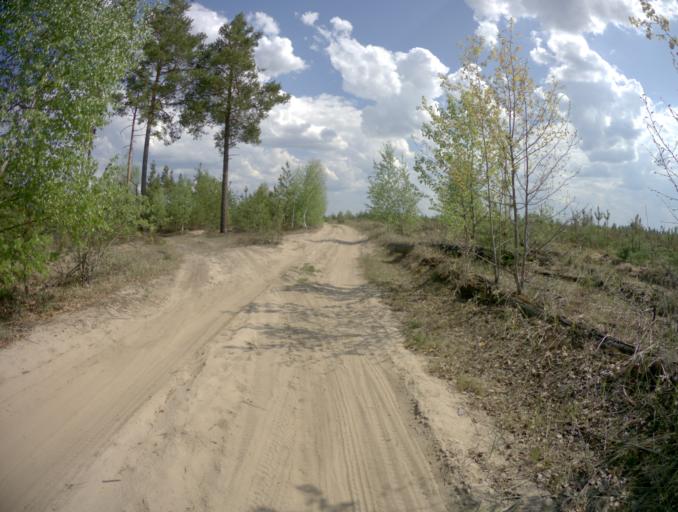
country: RU
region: Ivanovo
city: Talitsy
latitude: 56.4671
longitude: 42.1930
